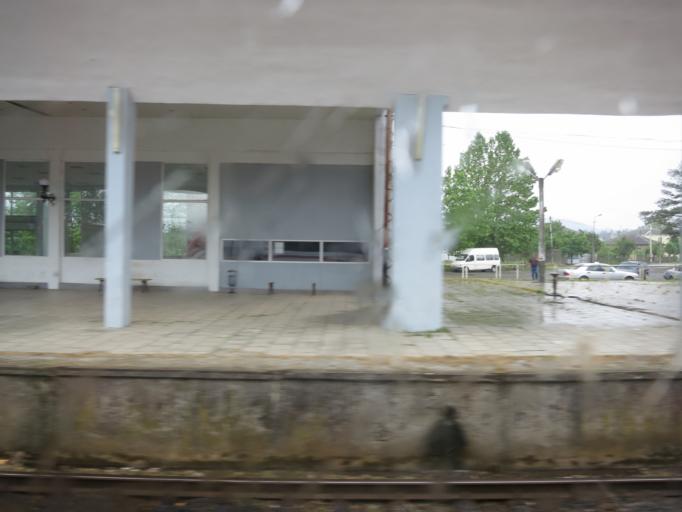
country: GE
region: Guria
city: Lanchkhuti
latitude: 42.0923
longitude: 42.0433
